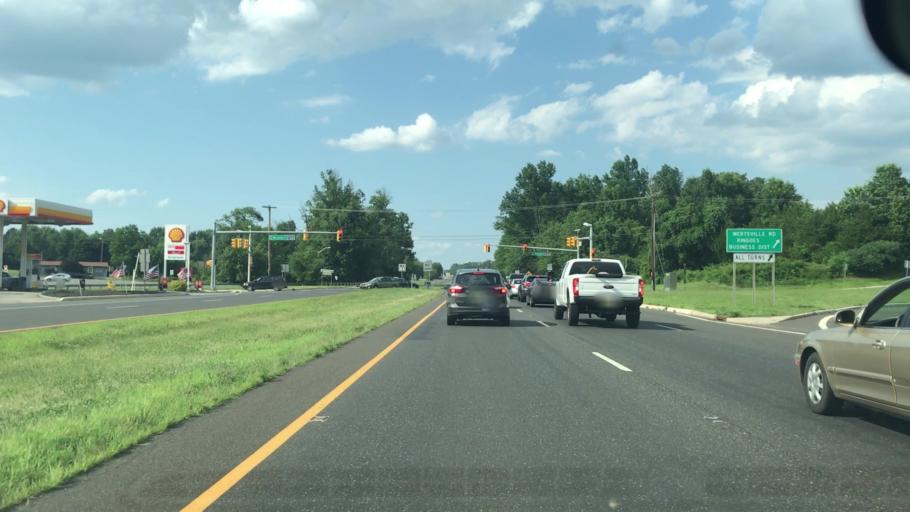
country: US
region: New Jersey
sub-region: Hunterdon County
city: Flemington
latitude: 40.4273
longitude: -74.8630
